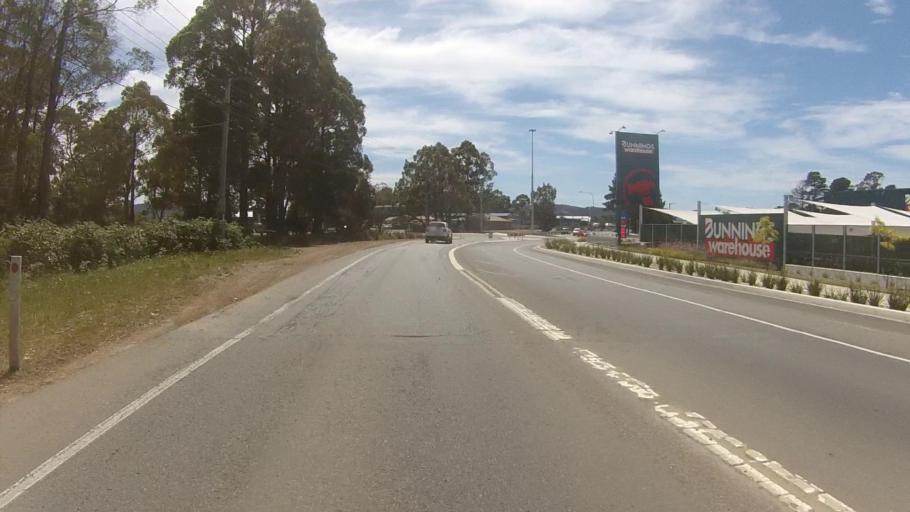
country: AU
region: Tasmania
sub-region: Kingborough
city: Kingston
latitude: -42.9849
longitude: 147.2915
